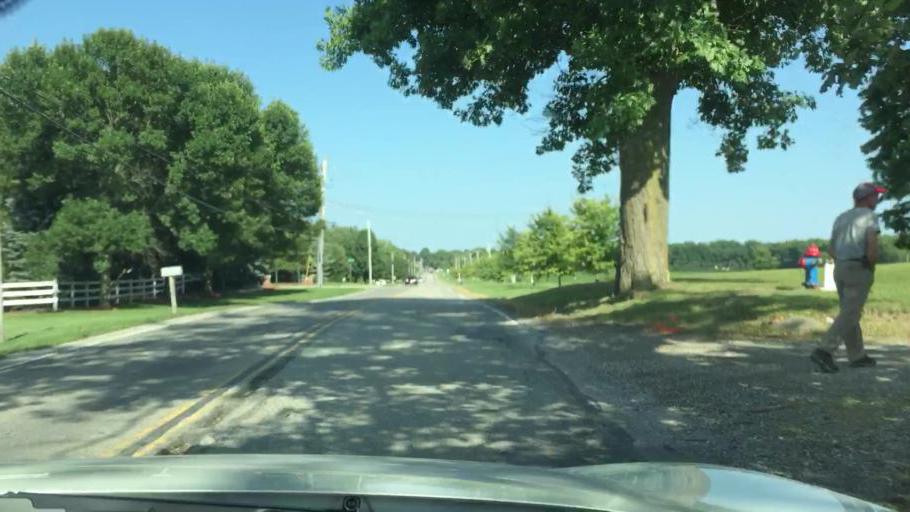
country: US
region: Ohio
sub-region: Union County
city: Marysville
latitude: 40.2283
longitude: -83.3957
